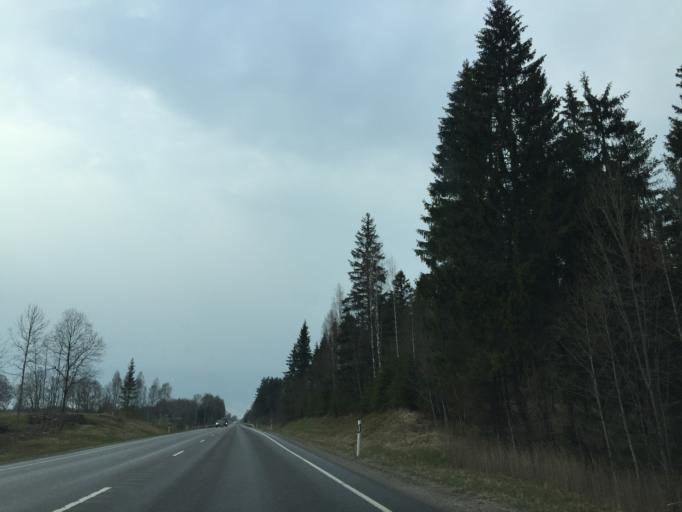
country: EE
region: Tartu
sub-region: UElenurme vald
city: Ulenurme
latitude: 58.1303
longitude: 26.7249
